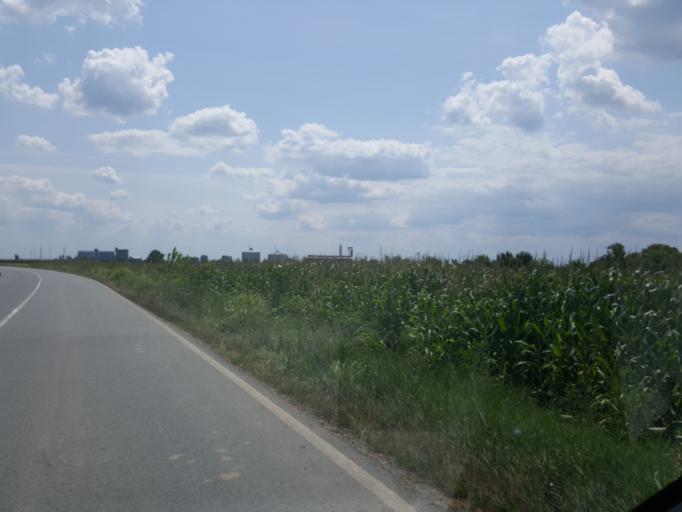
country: RS
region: Autonomna Pokrajina Vojvodina
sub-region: Sremski Okrug
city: Pecinci
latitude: 44.9031
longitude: 19.9565
